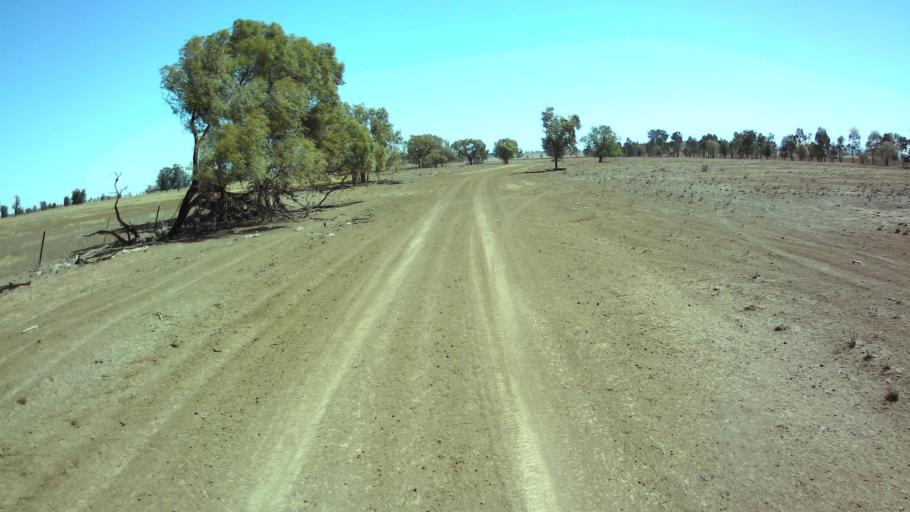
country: AU
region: New South Wales
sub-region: Forbes
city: Forbes
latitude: -33.7175
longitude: 147.6664
